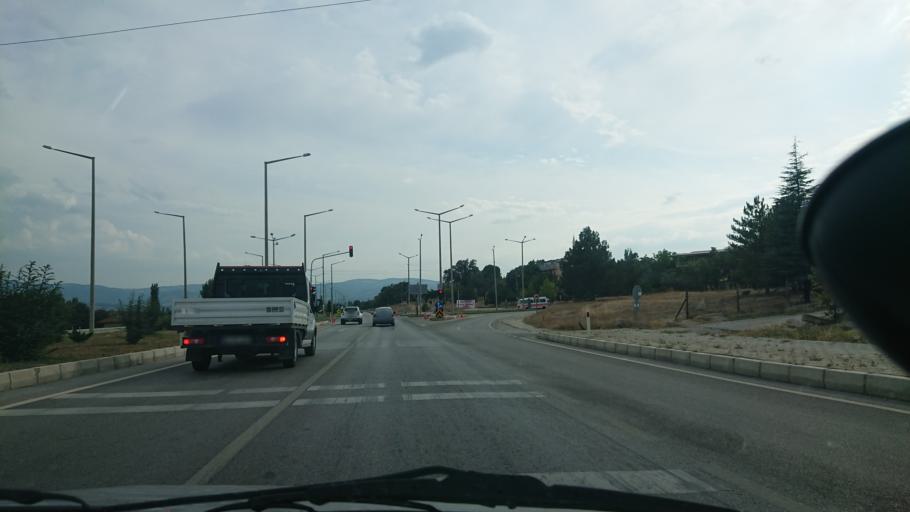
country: TR
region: Kuetahya
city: Gediz
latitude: 39.0008
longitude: 29.4036
